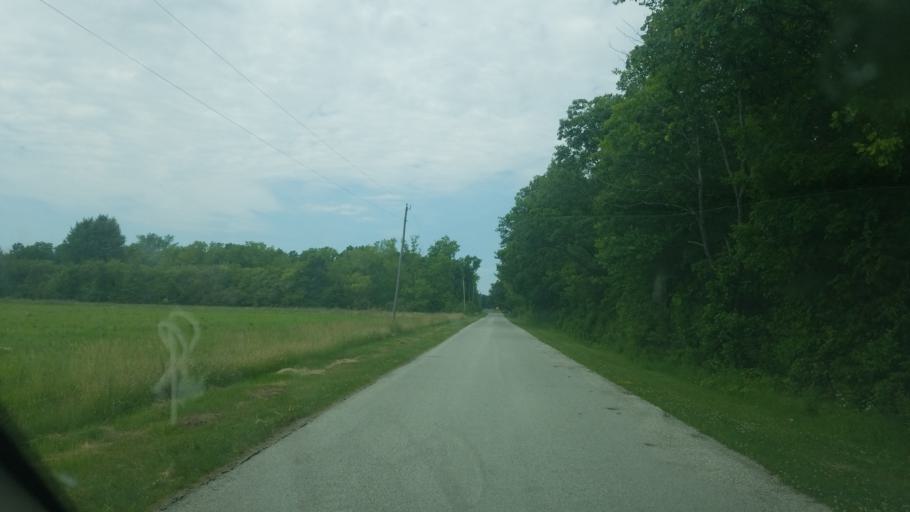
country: US
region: Ohio
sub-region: Wood County
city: North Baltimore
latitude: 41.2329
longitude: -83.6168
